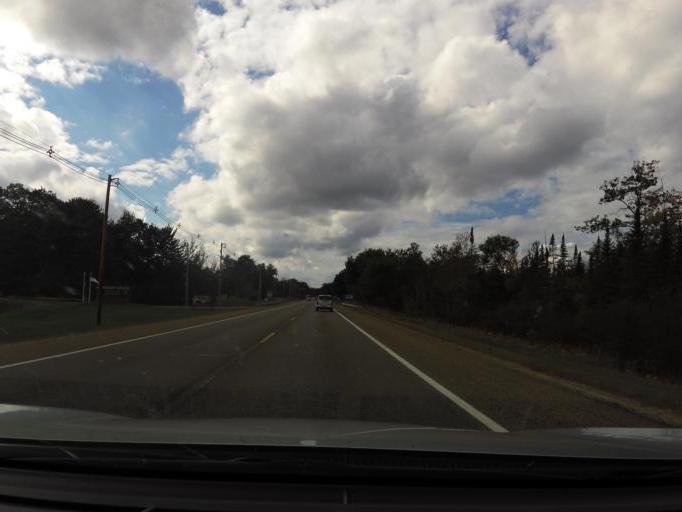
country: US
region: Michigan
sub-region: Roscommon County
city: Prudenville
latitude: 44.3058
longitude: -84.6292
